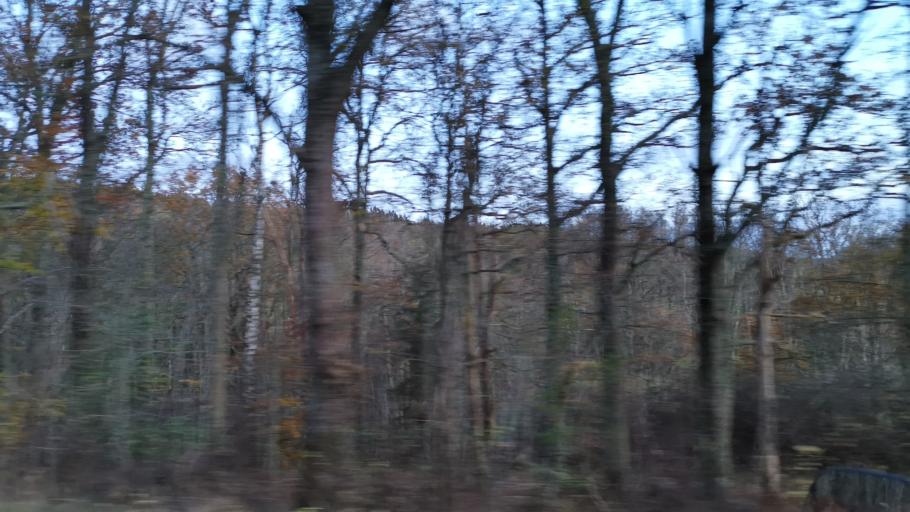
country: SE
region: Vaestra Goetaland
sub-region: Munkedals Kommun
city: Munkedal
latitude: 58.3992
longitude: 11.6539
